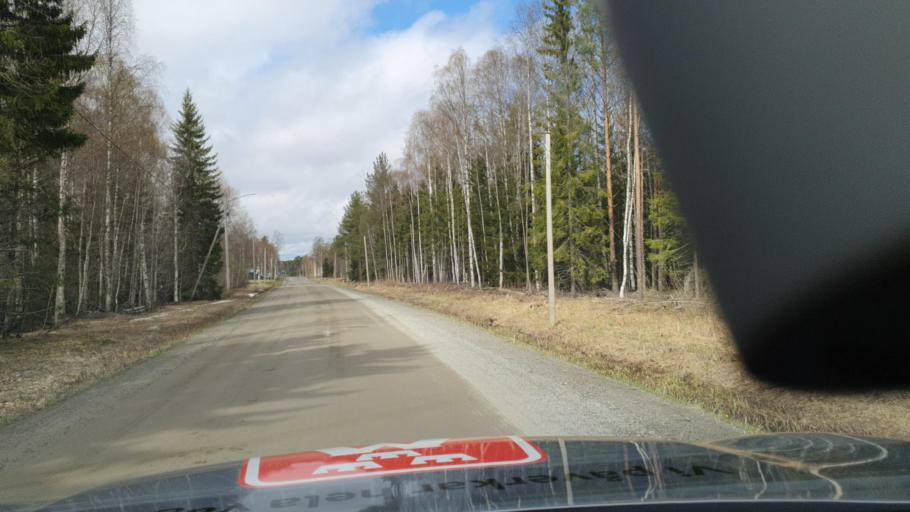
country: SE
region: Vaesterbotten
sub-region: Bjurholms Kommun
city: Bjurholm
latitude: 63.6942
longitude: 18.9571
